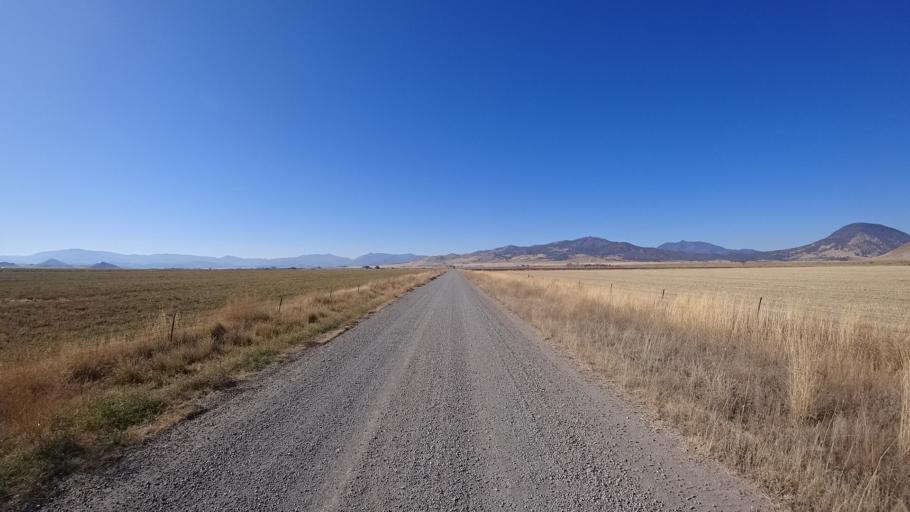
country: US
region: California
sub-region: Siskiyou County
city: Montague
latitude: 41.7865
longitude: -122.4480
